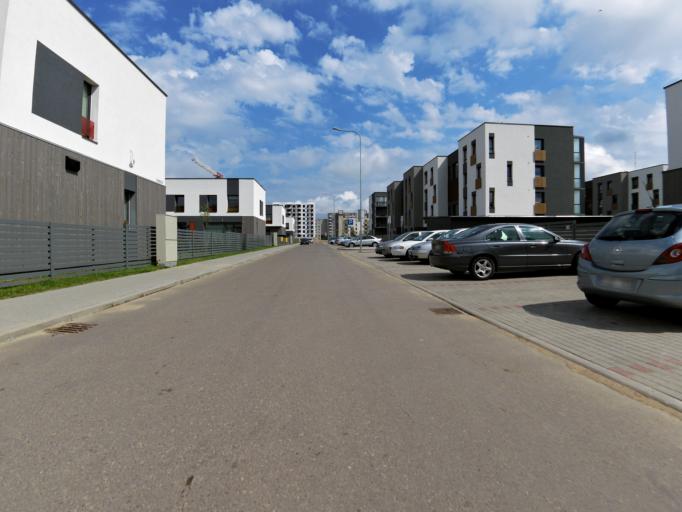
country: LT
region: Vilnius County
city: Pilaite
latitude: 54.7065
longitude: 25.1705
